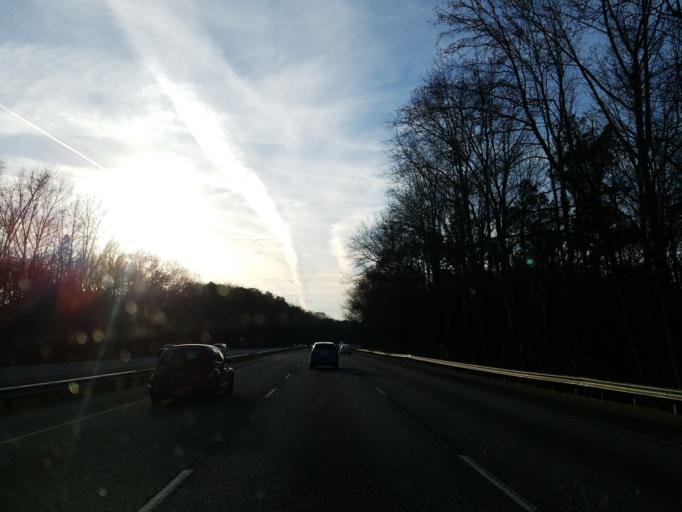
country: US
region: Georgia
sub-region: Douglas County
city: Douglasville
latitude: 33.7554
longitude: -84.6988
